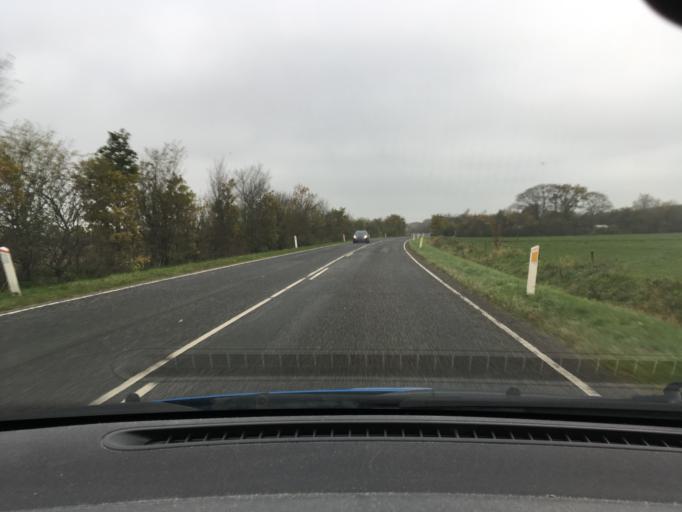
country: DK
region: South Denmark
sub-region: Aabenraa Kommune
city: Rodekro
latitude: 55.0707
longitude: 9.1920
